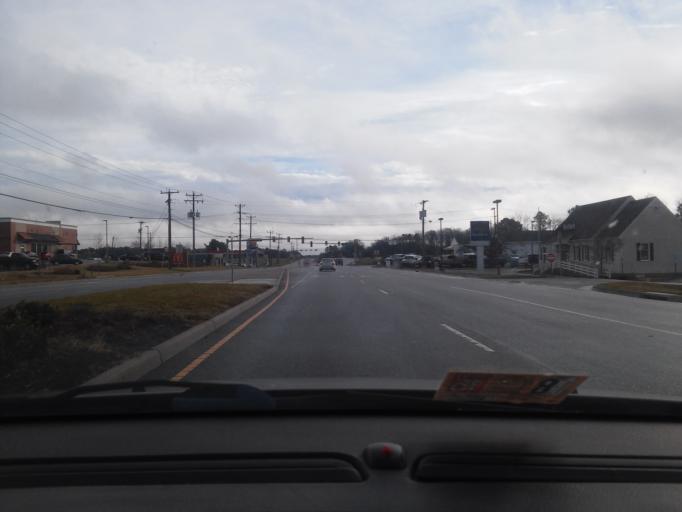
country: US
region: Virginia
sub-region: Henrico County
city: Short Pump
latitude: 37.6694
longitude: -77.6805
